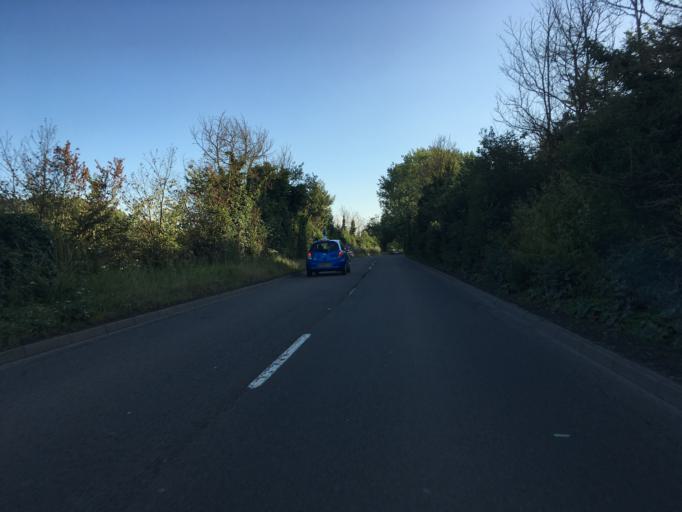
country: GB
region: England
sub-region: Hampshire
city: Tadley
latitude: 51.3961
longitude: -1.1420
